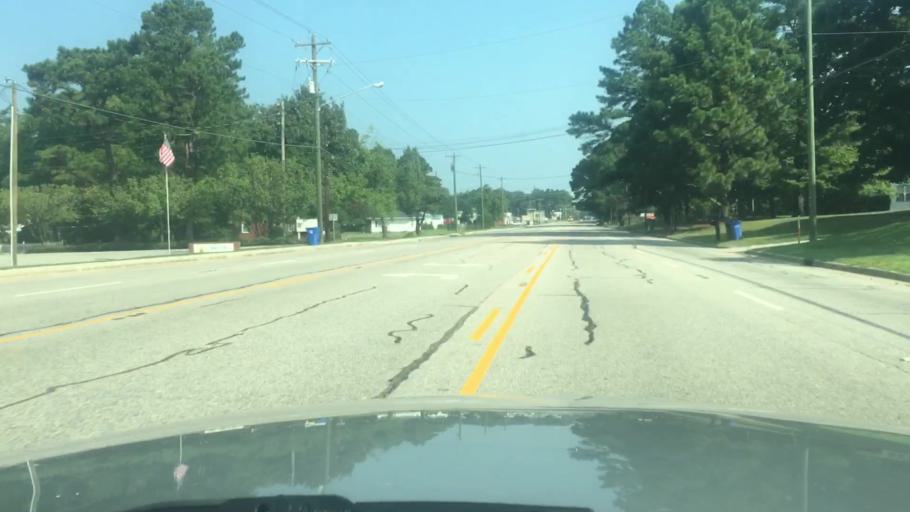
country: US
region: North Carolina
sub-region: Cumberland County
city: Fayetteville
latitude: 35.0245
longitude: -78.8420
